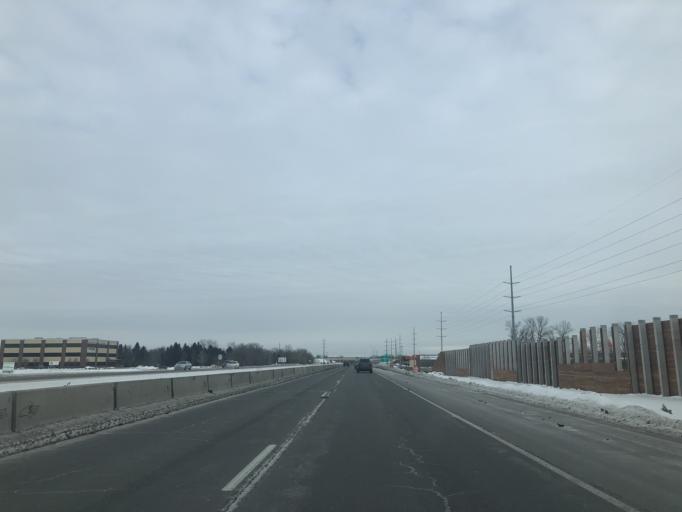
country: US
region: Minnesota
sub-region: Anoka County
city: Lexington
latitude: 45.1533
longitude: -93.1716
